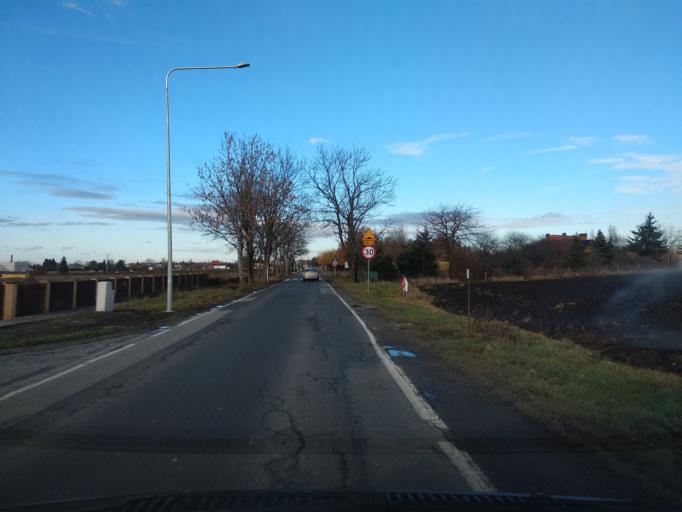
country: PL
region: Lower Silesian Voivodeship
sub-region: Powiat wroclawski
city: Zerniki Wroclawskie
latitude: 51.0461
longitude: 17.0378
